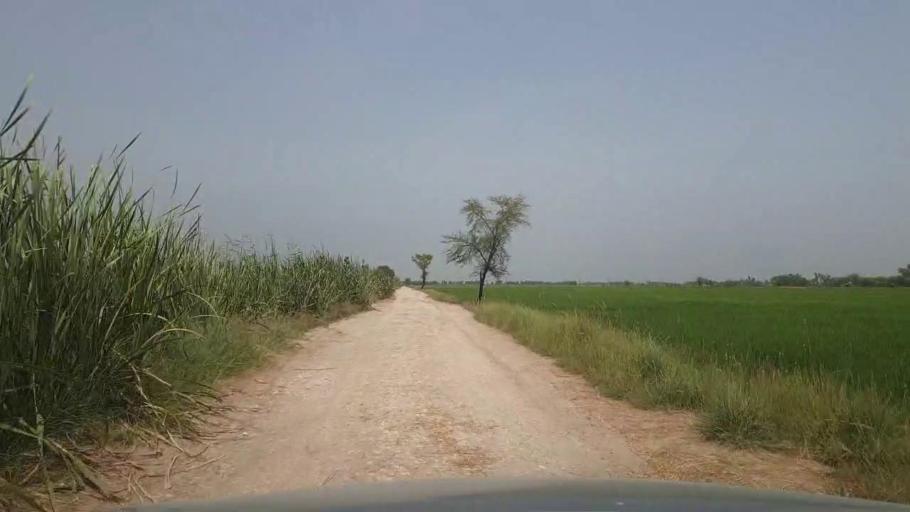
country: PK
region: Sindh
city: Garhi Yasin
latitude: 27.9336
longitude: 68.4320
